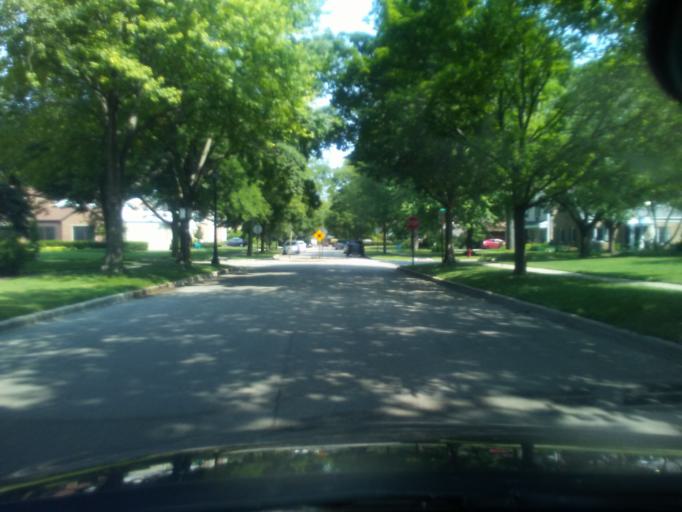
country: US
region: Illinois
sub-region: Cook County
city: Evanston
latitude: 42.0244
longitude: -87.6979
